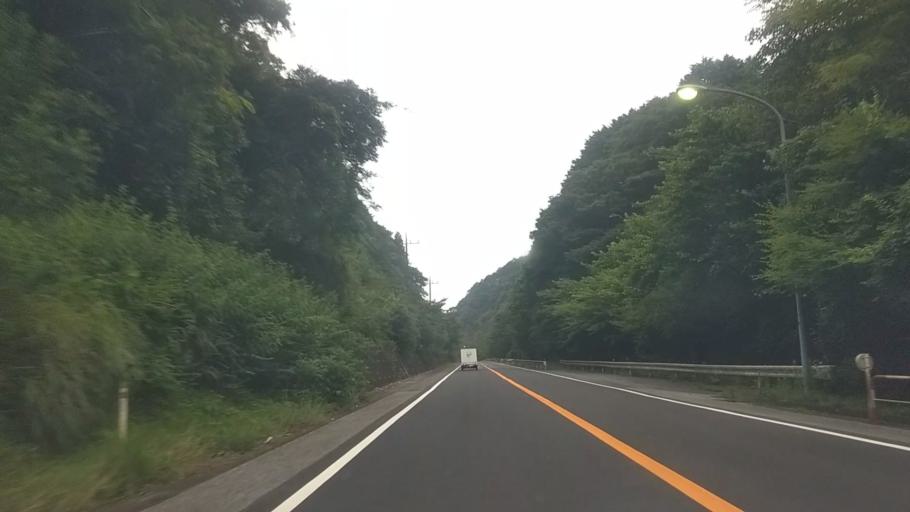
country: JP
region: Chiba
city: Kawaguchi
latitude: 35.1693
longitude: 140.0598
